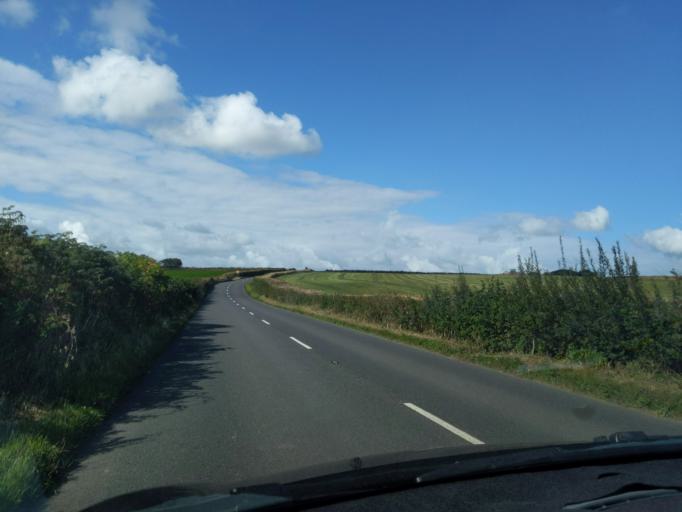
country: GB
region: England
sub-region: Devon
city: Holsworthy
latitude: 50.7459
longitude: -4.3241
